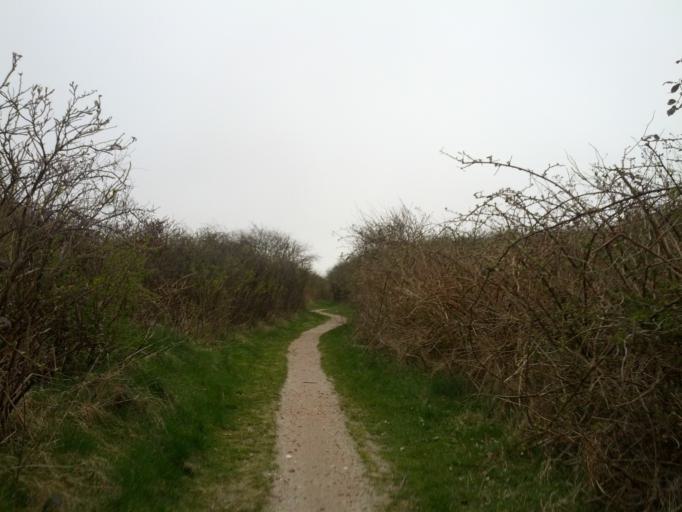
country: DE
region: Lower Saxony
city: Langeoog
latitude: 53.7375
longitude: 7.4704
